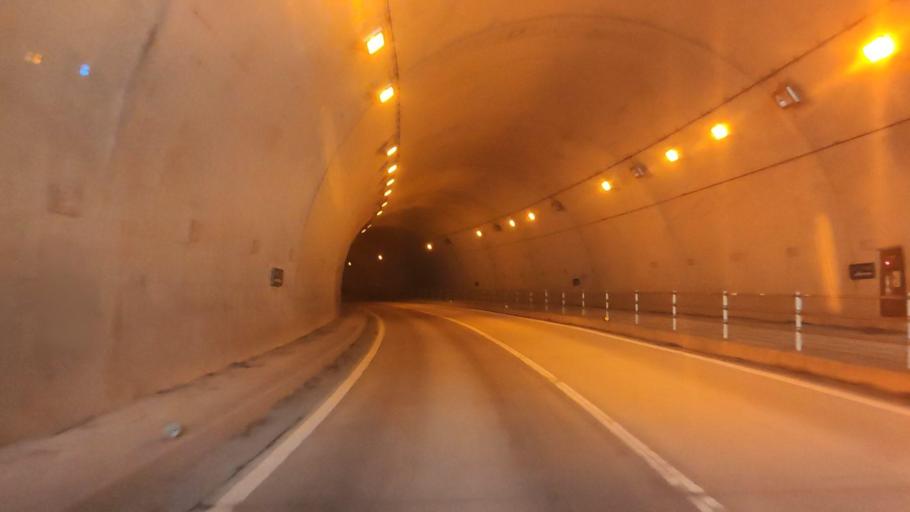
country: JP
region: Kumamoto
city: Hitoyoshi
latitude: 32.3932
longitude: 130.8276
